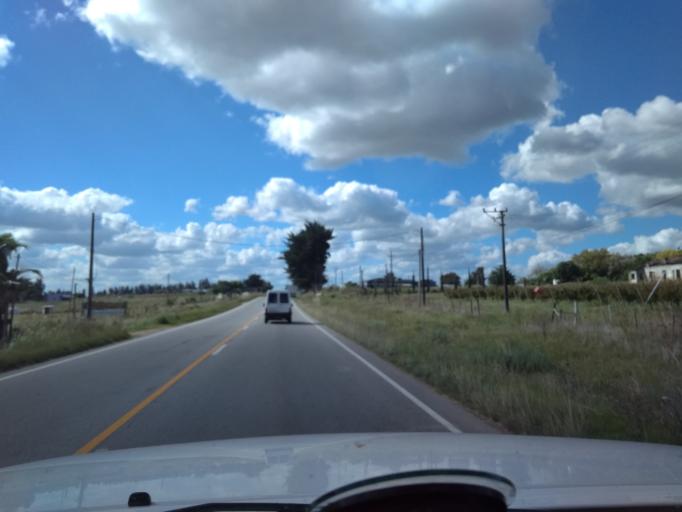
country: UY
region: Canelones
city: Sauce
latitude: -34.6904
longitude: -56.0545
